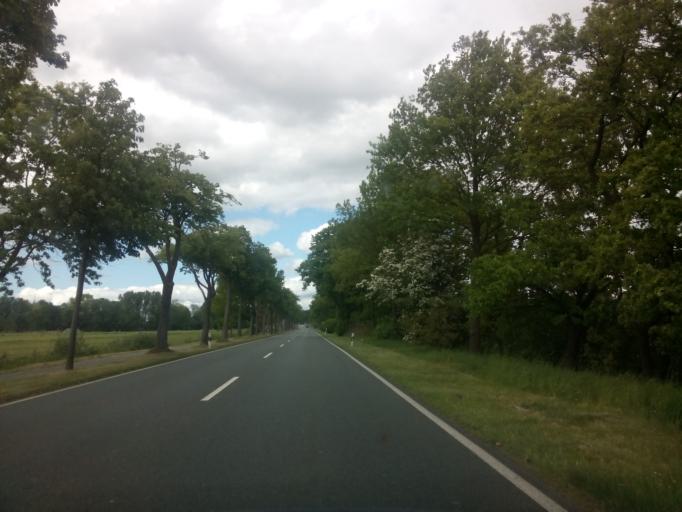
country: DE
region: Lower Saxony
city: Ritterhude
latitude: 53.1586
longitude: 8.7479
